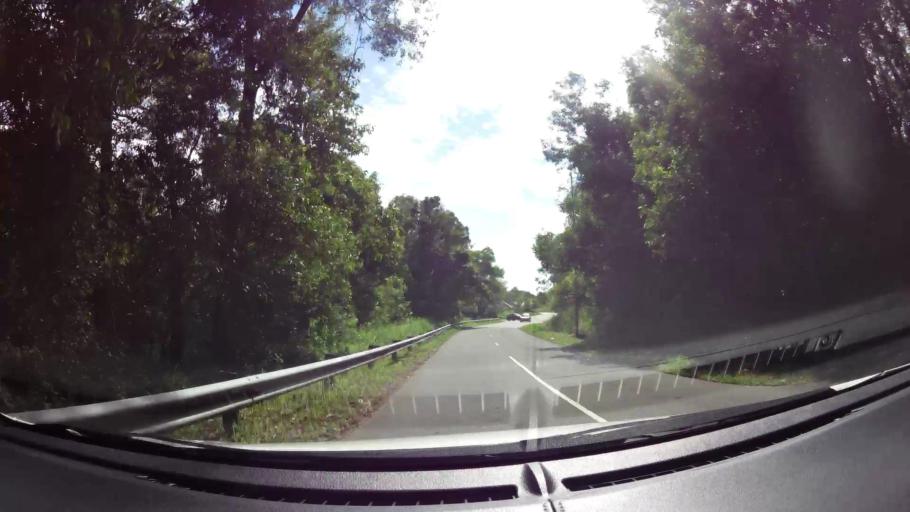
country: BN
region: Brunei and Muara
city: Bandar Seri Begawan
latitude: 4.9295
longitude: 114.9066
